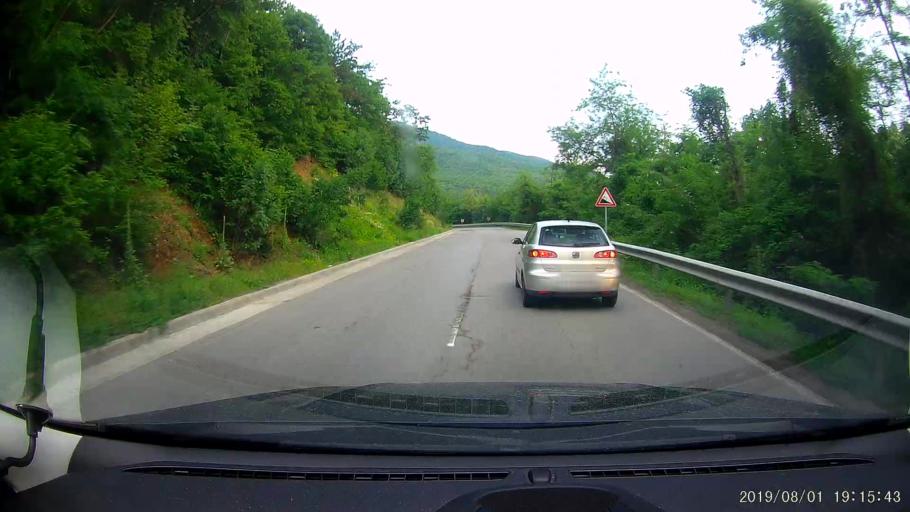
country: BG
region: Shumen
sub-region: Obshtina Smyadovo
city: Smyadovo
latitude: 42.9302
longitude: 26.9442
